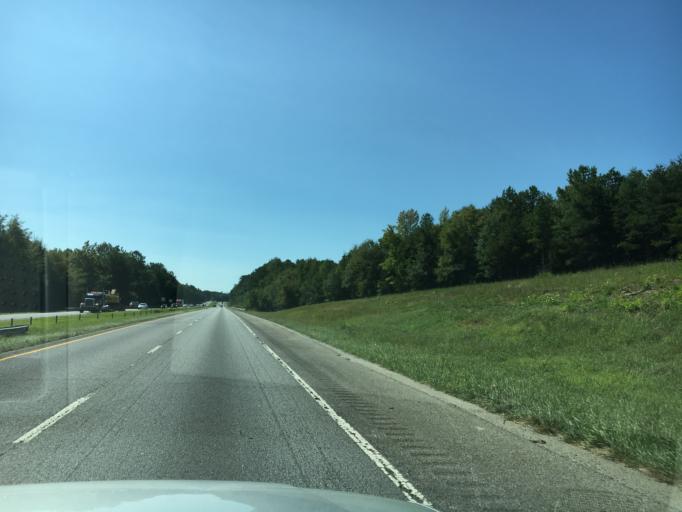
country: US
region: South Carolina
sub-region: Spartanburg County
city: Roebuck
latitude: 34.7872
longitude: -81.9556
